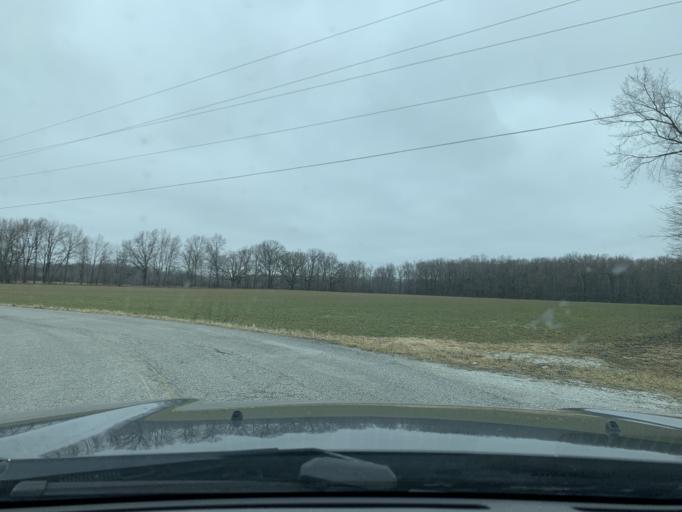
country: US
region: Indiana
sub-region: Porter County
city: Chesterton
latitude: 41.6105
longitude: -87.0045
